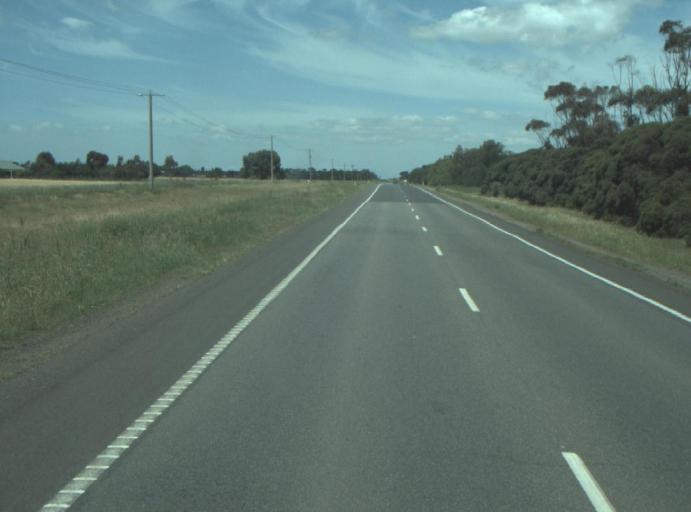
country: AU
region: Victoria
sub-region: Greater Geelong
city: Lara
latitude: -38.0089
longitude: 144.3503
